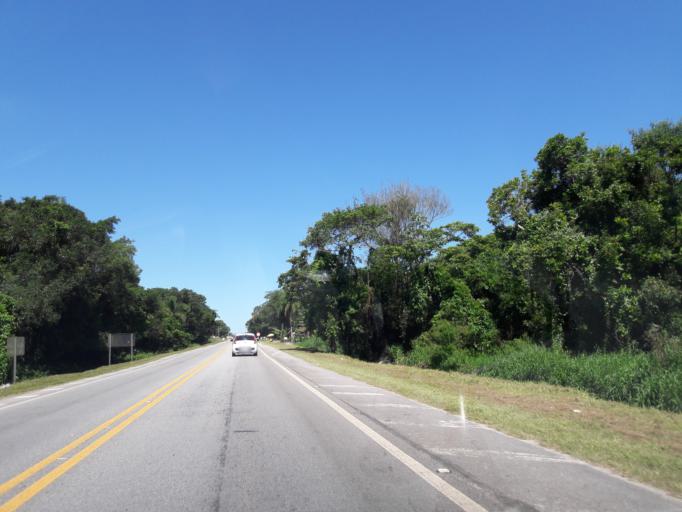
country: BR
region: Parana
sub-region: Pontal Do Parana
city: Pontal do Parana
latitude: -25.6880
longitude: -48.4897
